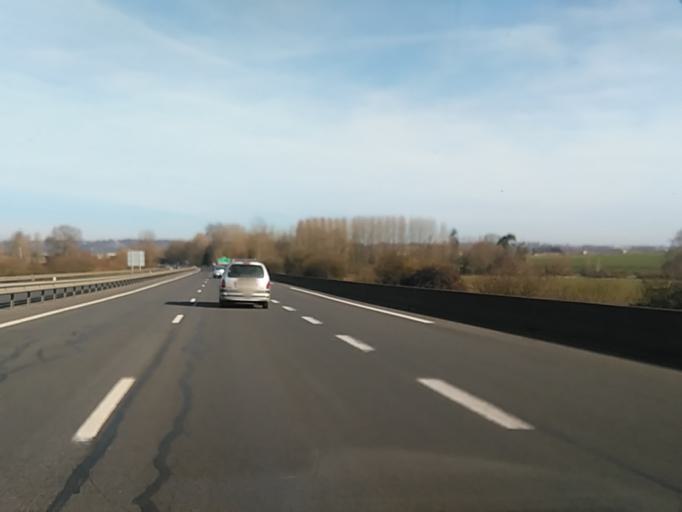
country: FR
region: Lower Normandy
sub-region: Departement de la Manche
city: Saint-Quentin-sur-le-Homme
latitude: 48.6354
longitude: -1.3415
